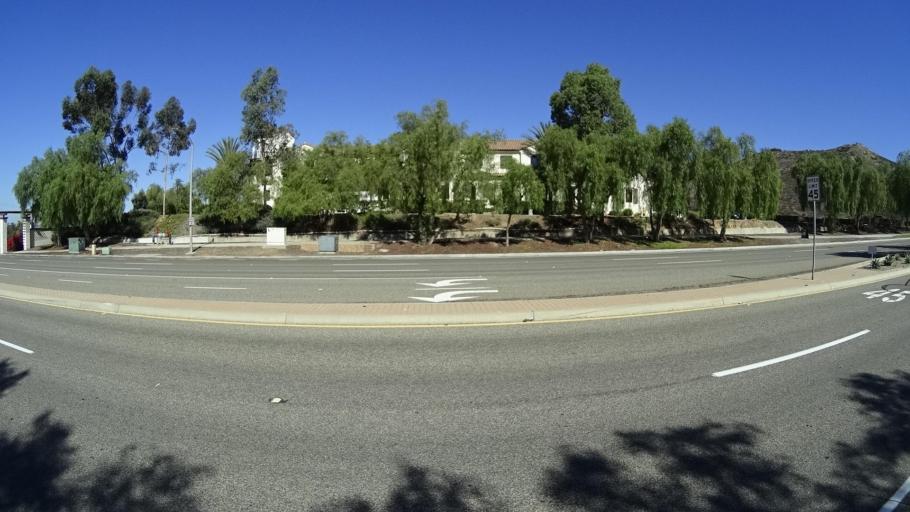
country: US
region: California
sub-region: San Diego County
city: La Presa
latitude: 32.6619
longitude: -116.9706
